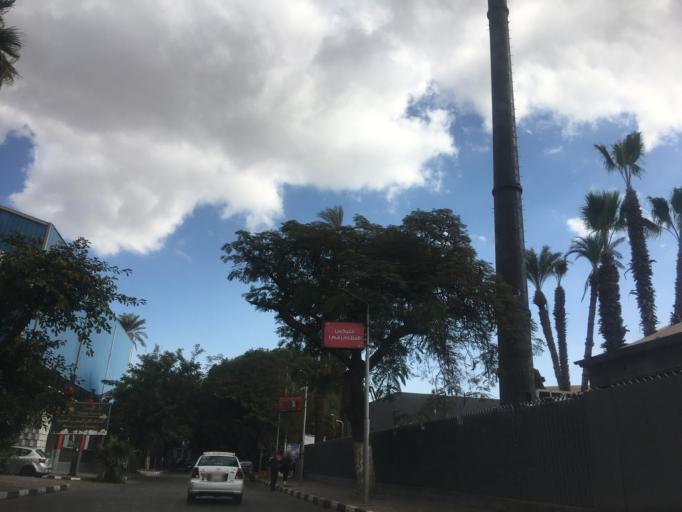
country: EG
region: Muhafazat al Qahirah
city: Cairo
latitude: 30.0438
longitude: 31.2227
